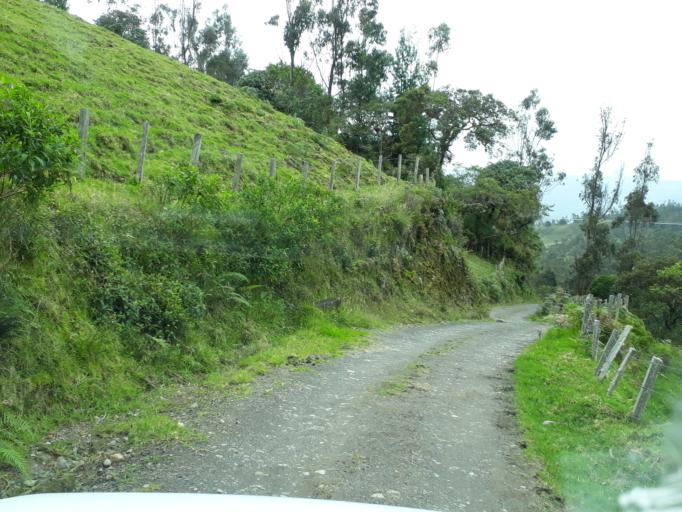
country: CO
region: Cundinamarca
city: Junin
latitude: 4.7490
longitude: -73.6287
